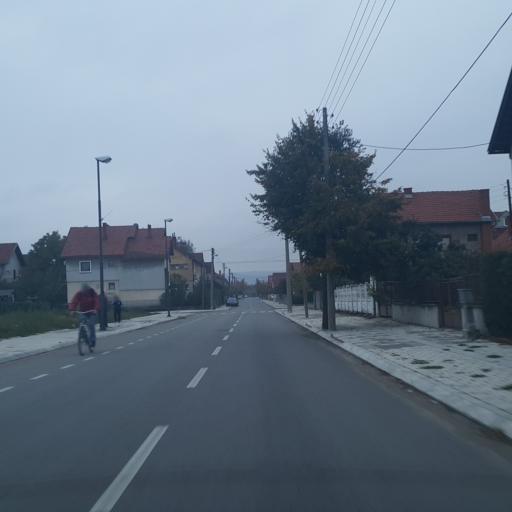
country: RS
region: Central Serbia
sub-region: Zajecarski Okrug
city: Zajecar
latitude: 43.9055
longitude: 22.2612
